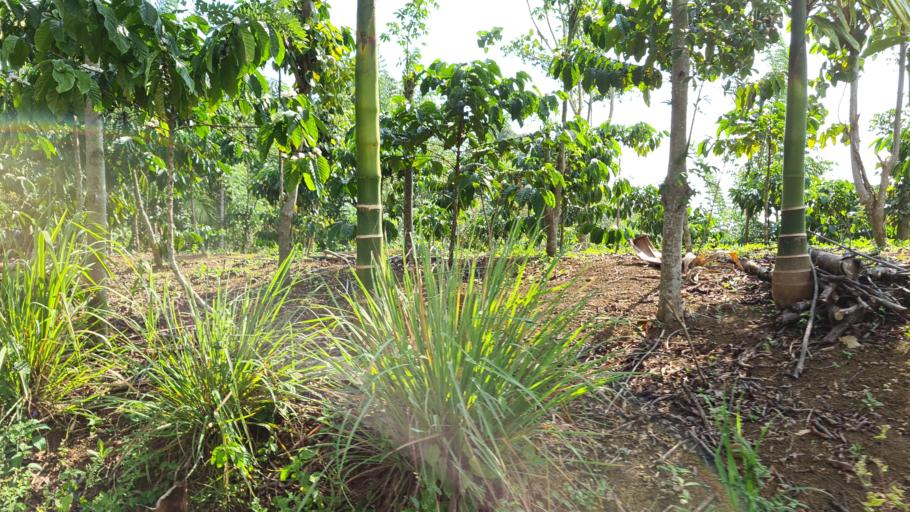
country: ID
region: Lampung
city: Kuripan
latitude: -5.0697
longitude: 103.8736
